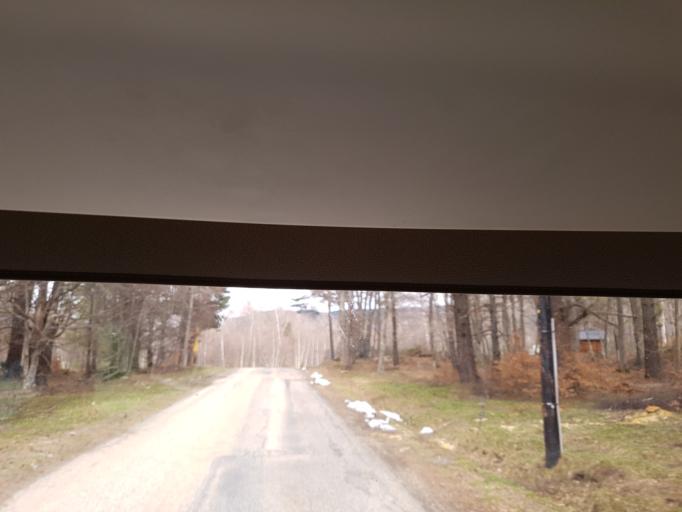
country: FR
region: Languedoc-Roussillon
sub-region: Departement de l'Aude
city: Quillan
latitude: 42.6830
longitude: 2.1235
